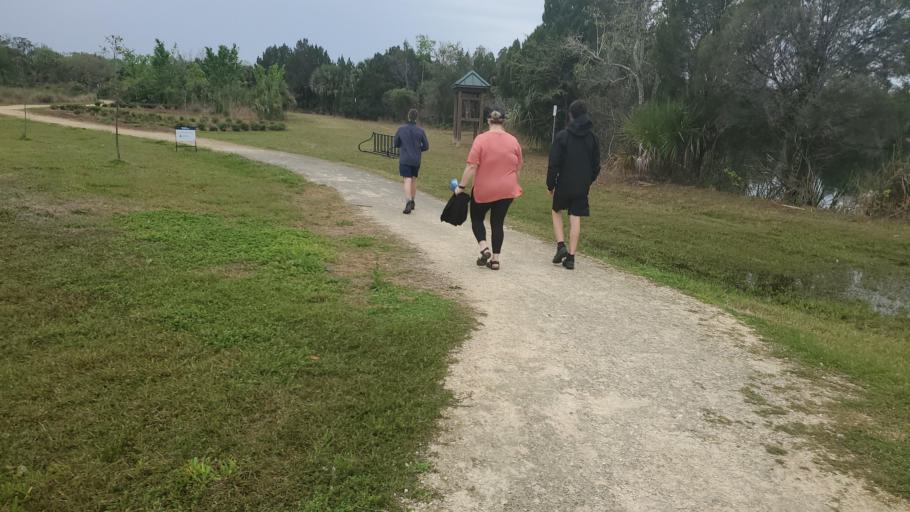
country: US
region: Florida
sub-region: Citrus County
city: Crystal River
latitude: 28.8912
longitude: -82.5879
